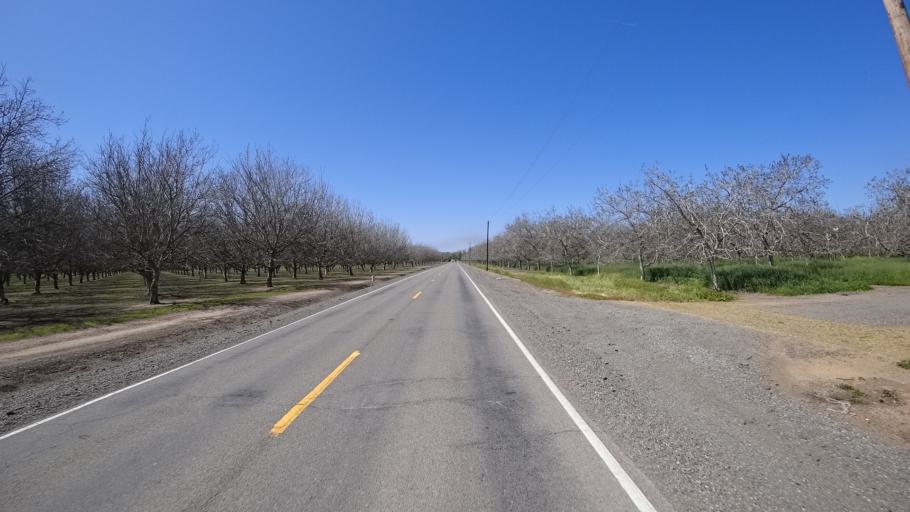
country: US
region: California
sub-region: Glenn County
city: Willows
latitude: 39.4644
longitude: -121.9826
